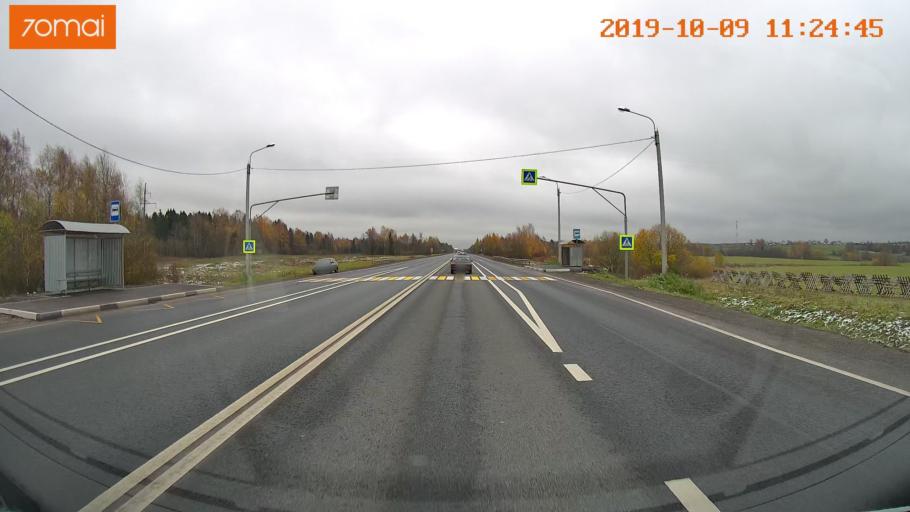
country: RU
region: Vologda
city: Vologda
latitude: 59.1083
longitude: 39.9834
